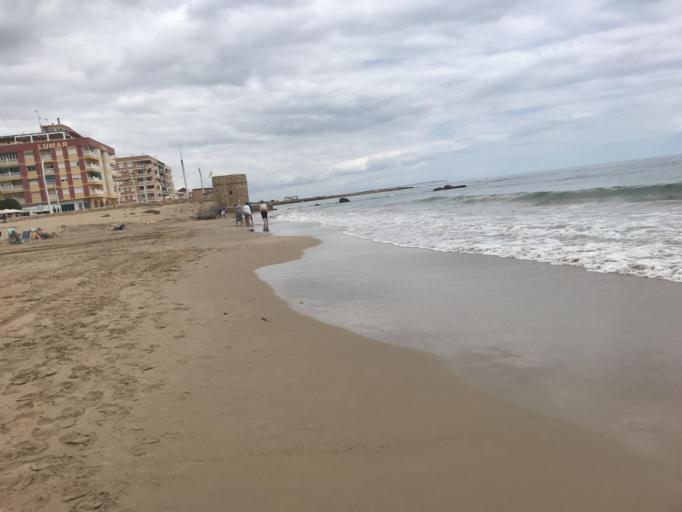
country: ES
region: Valencia
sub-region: Provincia de Alicante
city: Torrevieja
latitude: 38.0254
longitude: -0.6528
